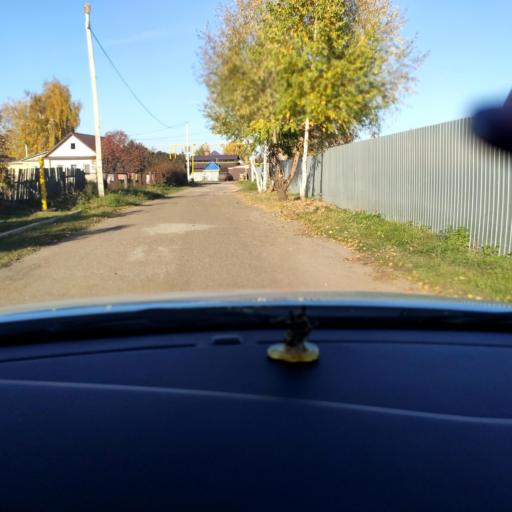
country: RU
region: Tatarstan
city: Stolbishchi
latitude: 55.6246
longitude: 49.1507
